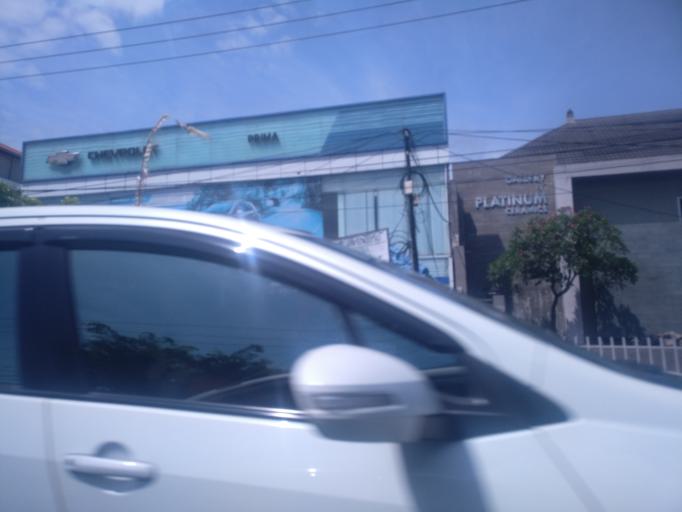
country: ID
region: Bali
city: Banjar Kertasari
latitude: -8.6366
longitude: 115.1959
